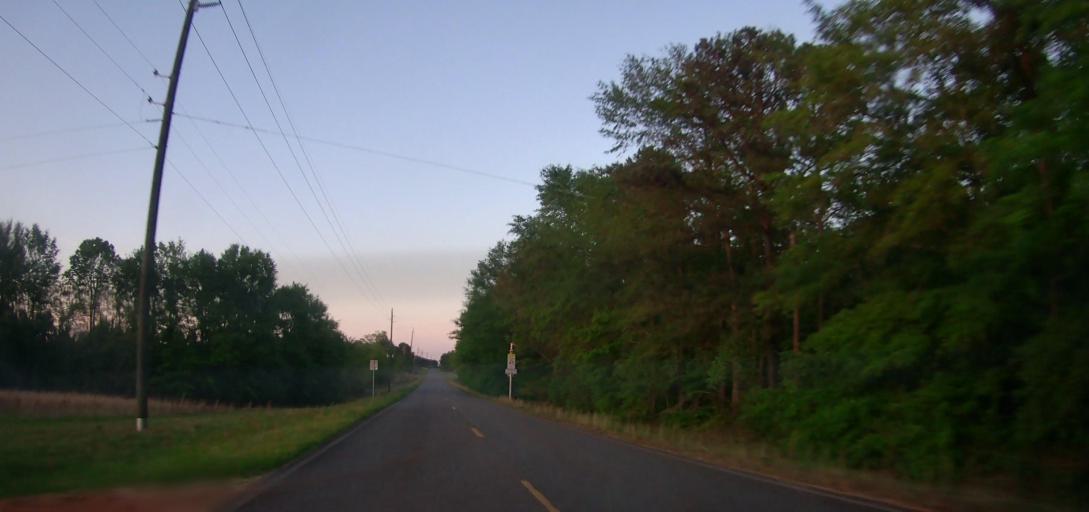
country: US
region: Georgia
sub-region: Marion County
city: Buena Vista
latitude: 32.2852
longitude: -84.5395
